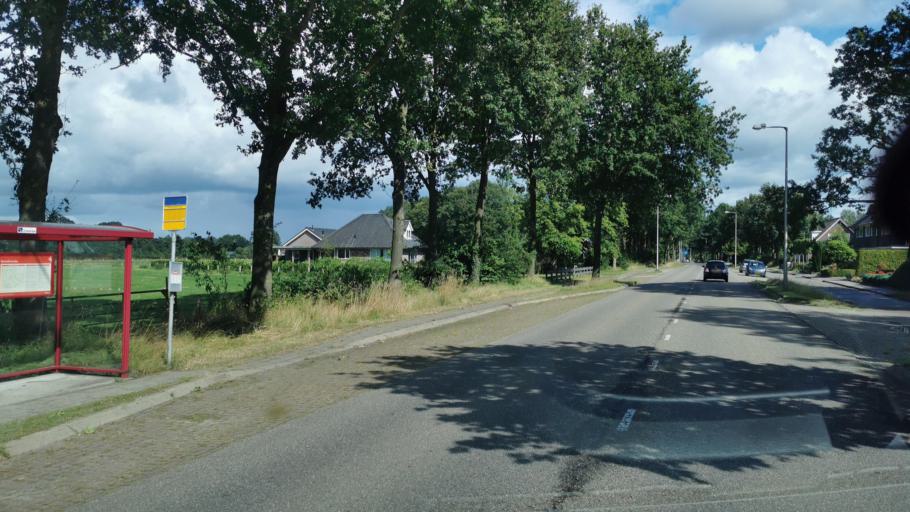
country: NL
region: Overijssel
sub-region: Gemeente Losser
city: Losser
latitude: 52.2618
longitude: 6.9846
